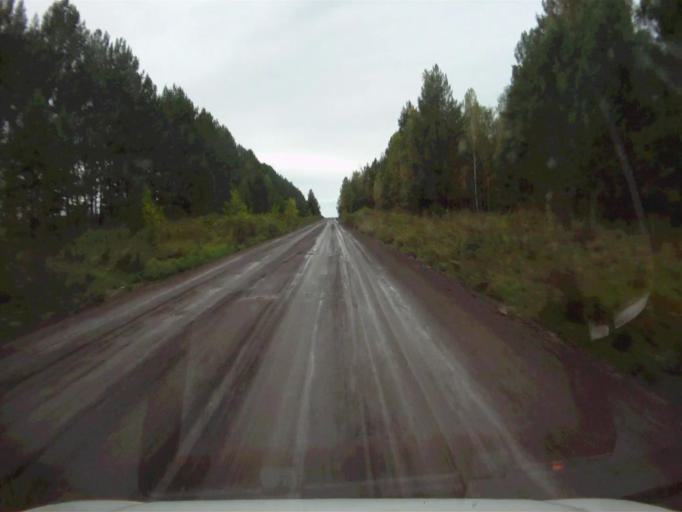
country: RU
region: Chelyabinsk
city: Nyazepetrovsk
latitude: 56.1409
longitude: 59.2933
